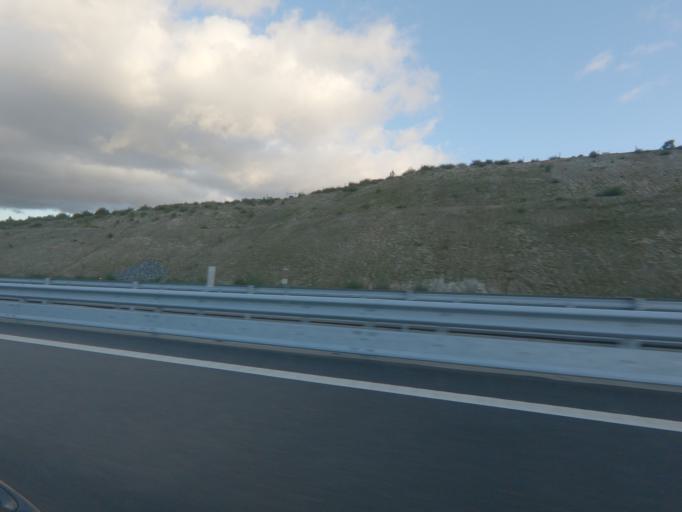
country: PT
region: Vila Real
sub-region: Vila Real
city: Vila Real
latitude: 41.2712
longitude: -7.7826
